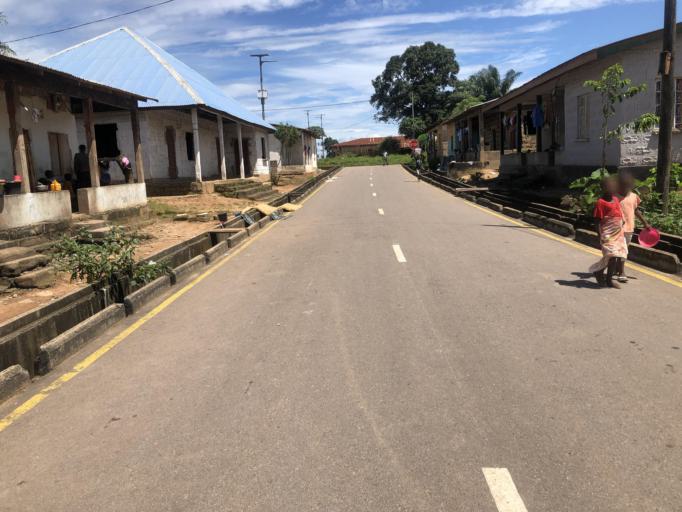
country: SL
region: Eastern Province
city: Koidu
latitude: 8.6465
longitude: -10.9600
